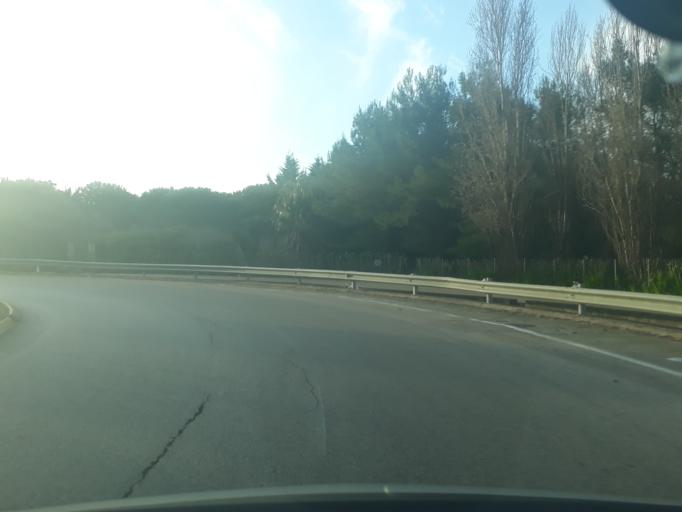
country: IT
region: Apulia
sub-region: Provincia di Brindisi
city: Brindisi
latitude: 40.6575
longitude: 17.9284
